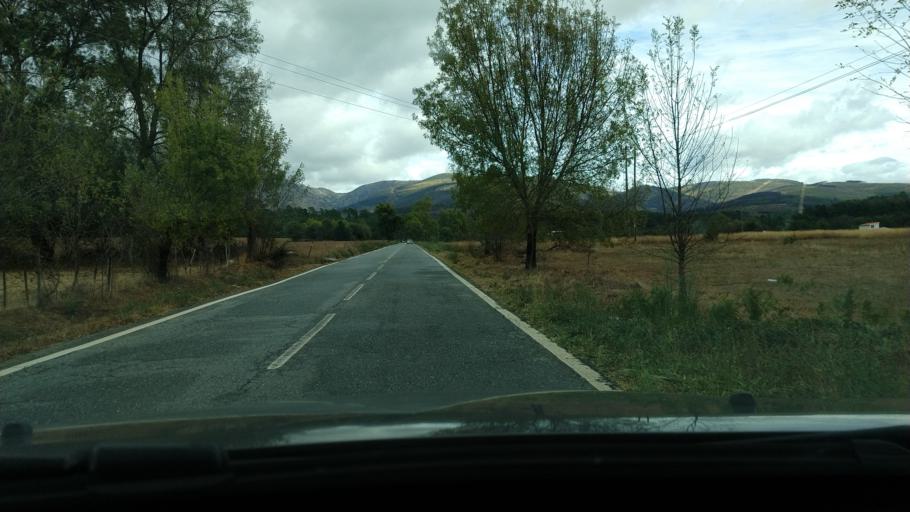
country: PT
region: Castelo Branco
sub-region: Covilha
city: Covilha
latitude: 40.2331
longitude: -7.6023
